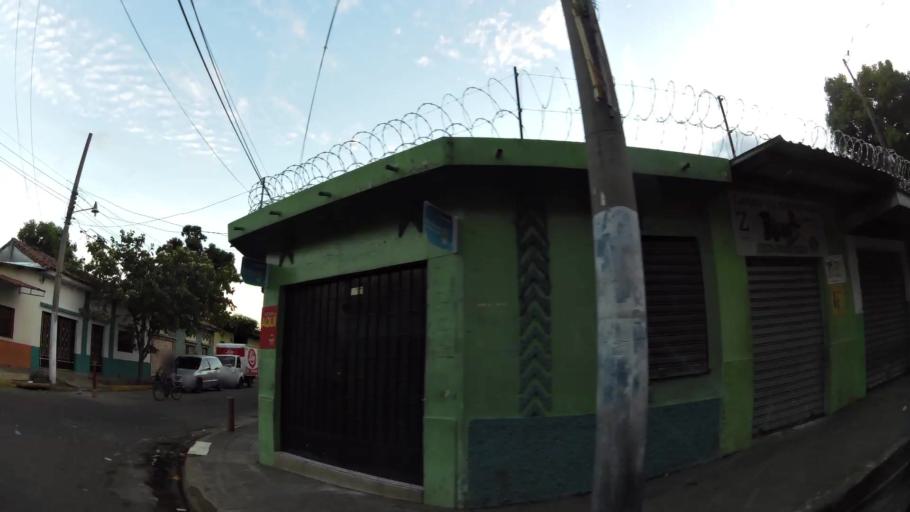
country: SV
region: San Vicente
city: San Vicente
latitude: 13.6430
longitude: -88.7886
